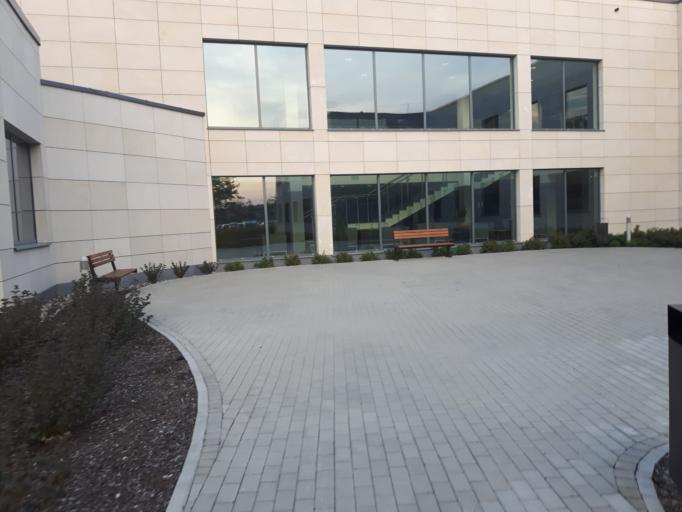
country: PL
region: Masovian Voivodeship
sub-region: Powiat wolominski
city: Zabki
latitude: 52.2990
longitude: 21.1119
